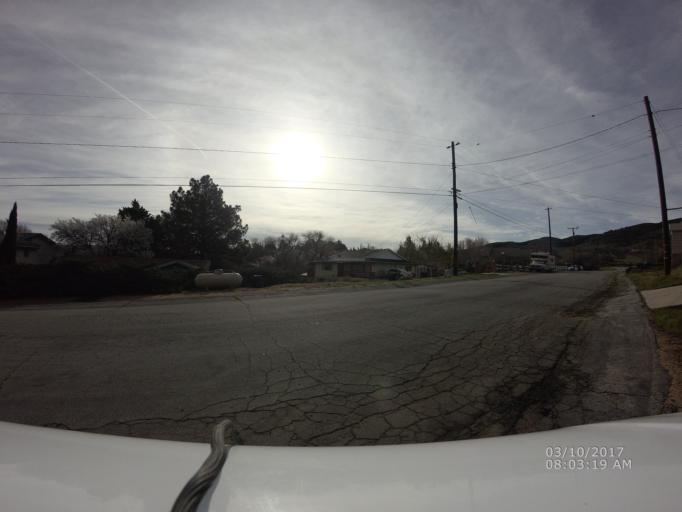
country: US
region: California
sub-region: Los Angeles County
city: Green Valley
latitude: 34.6620
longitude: -118.4013
